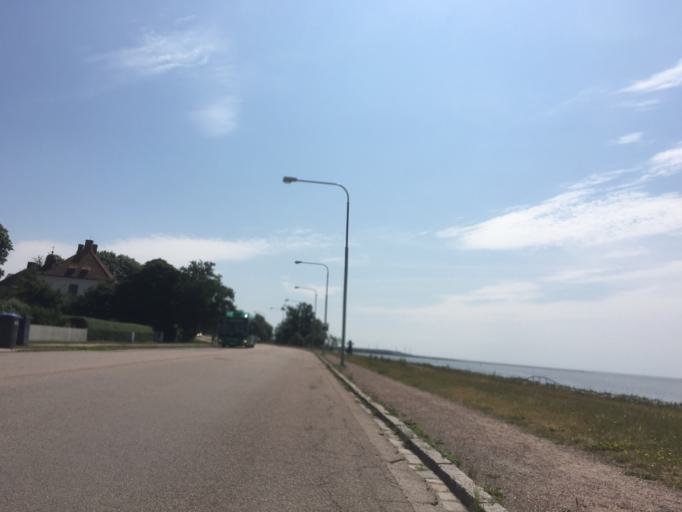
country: SE
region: Skane
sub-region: Landskrona
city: Landskrona
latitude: 55.8864
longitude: 12.8112
